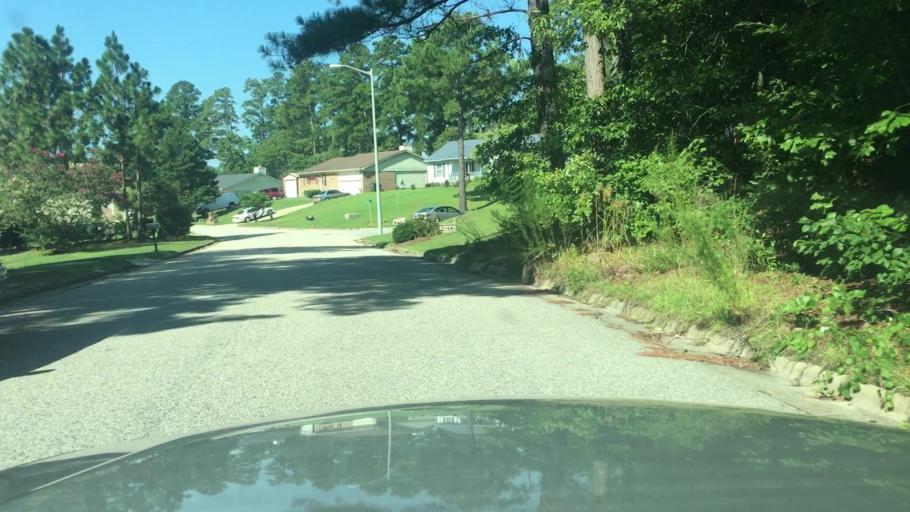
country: US
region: North Carolina
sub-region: Cumberland County
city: Fayetteville
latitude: 35.1081
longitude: -78.9059
